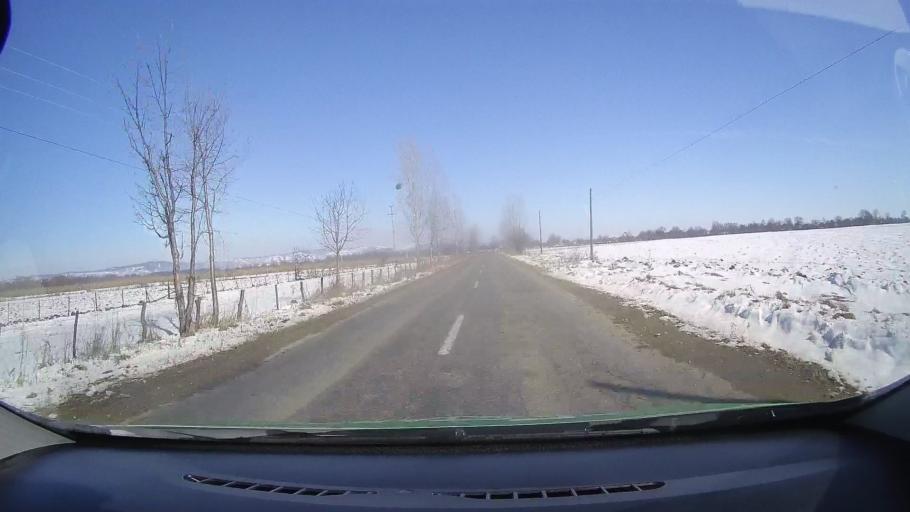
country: RO
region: Brasov
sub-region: Oras Victoria
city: Victoria
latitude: 45.7381
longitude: 24.7340
